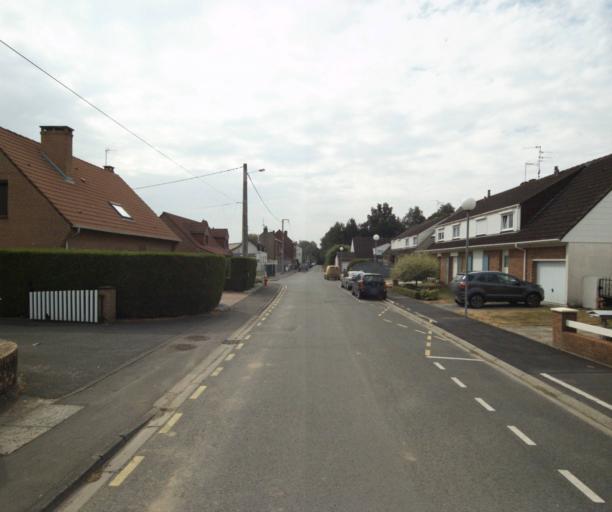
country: FR
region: Nord-Pas-de-Calais
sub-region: Departement du Nord
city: Santes
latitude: 50.5928
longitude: 2.9681
